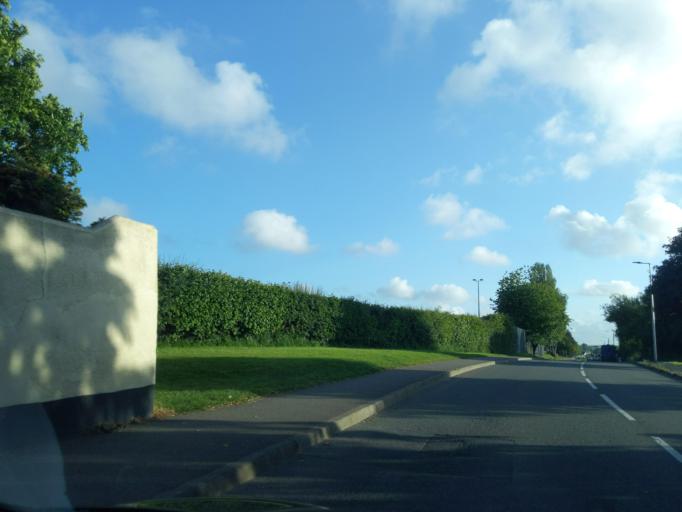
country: GB
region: England
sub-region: Devon
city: Great Torrington
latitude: 50.9571
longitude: -4.1316
